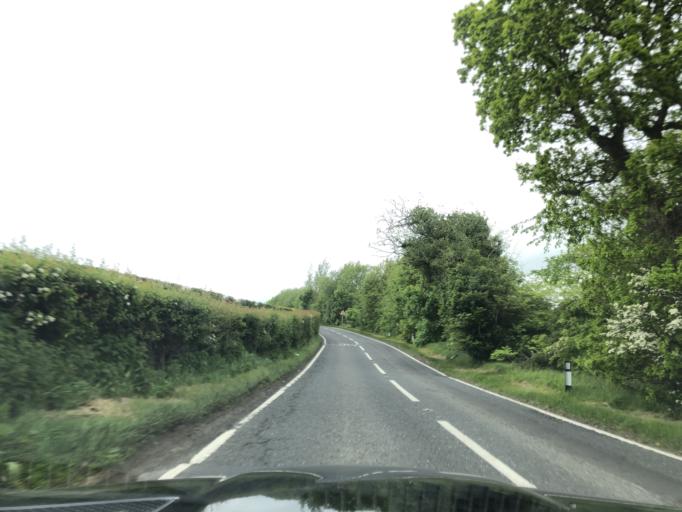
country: GB
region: Northern Ireland
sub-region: Down District
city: Downpatrick
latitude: 54.3550
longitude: -5.7410
